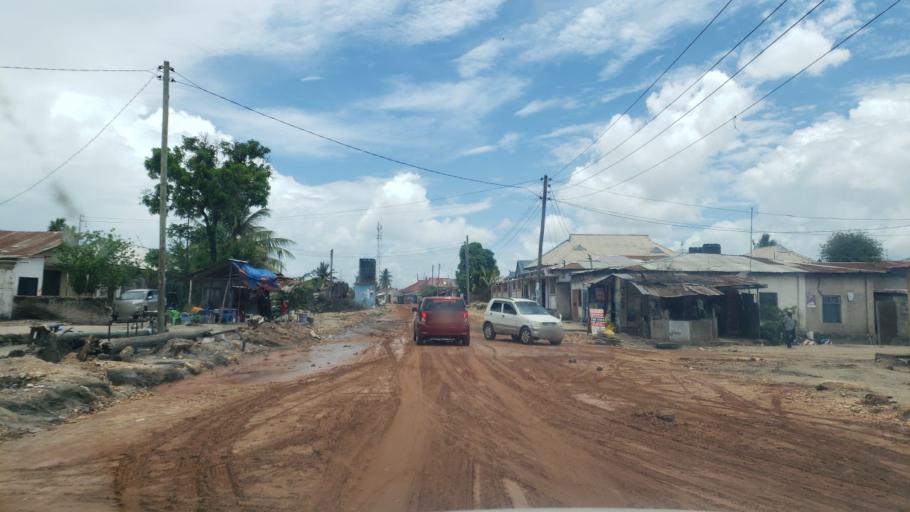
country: TZ
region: Dar es Salaam
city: Magomeni
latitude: -6.8111
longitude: 39.2526
